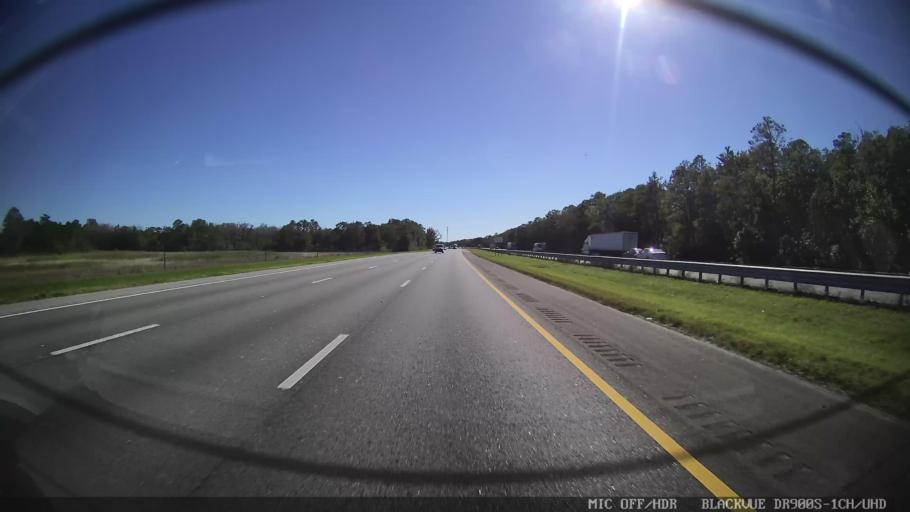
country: US
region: Florida
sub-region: Pasco County
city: Wesley Chapel
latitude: 28.2933
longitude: -82.3264
